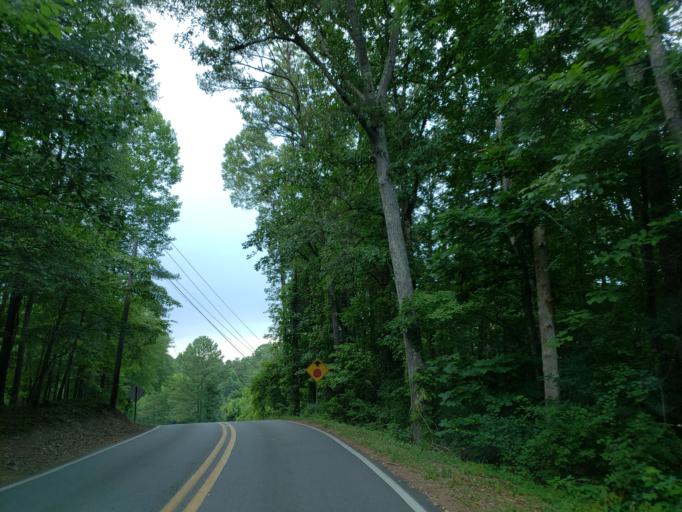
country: US
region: Georgia
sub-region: Cherokee County
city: Holly Springs
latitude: 34.1308
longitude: -84.4524
